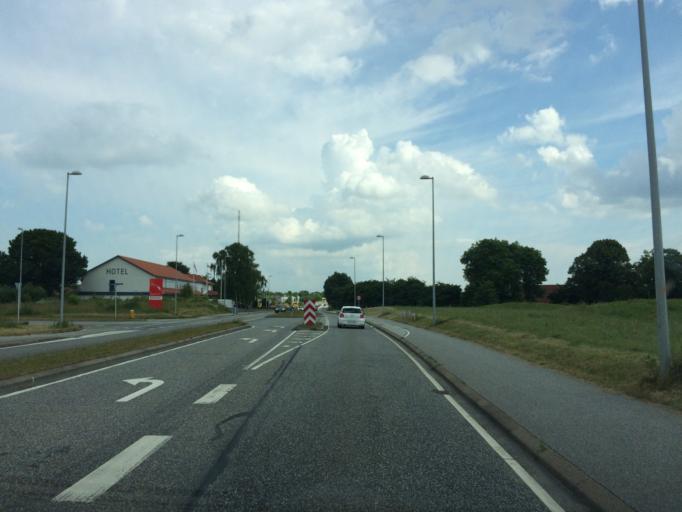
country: DK
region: South Denmark
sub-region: Fredericia Kommune
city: Snoghoj
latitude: 55.5297
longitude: 9.7068
